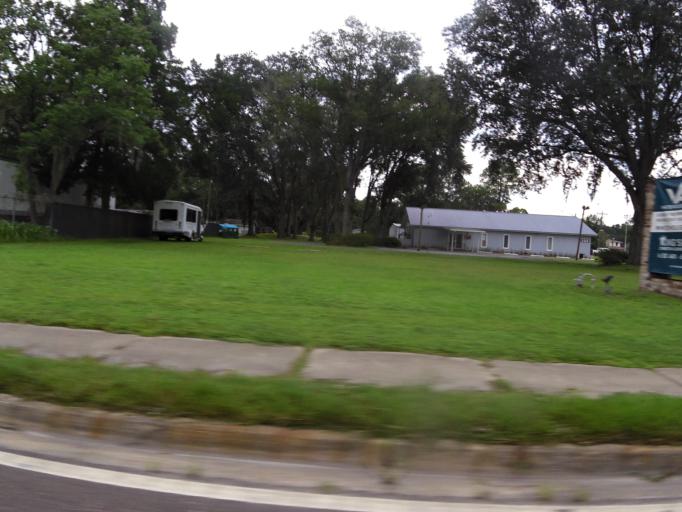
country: US
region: Florida
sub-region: Duval County
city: Baldwin
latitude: 30.3130
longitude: -81.8485
